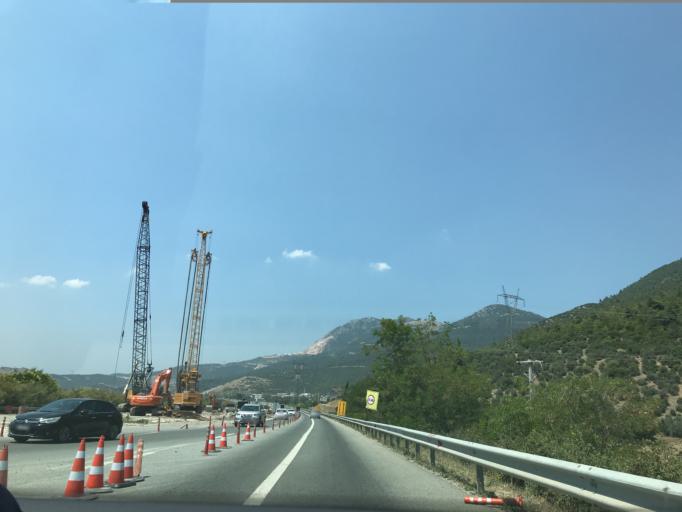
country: TR
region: Bursa
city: Kestel
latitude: 40.2403
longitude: 29.2609
